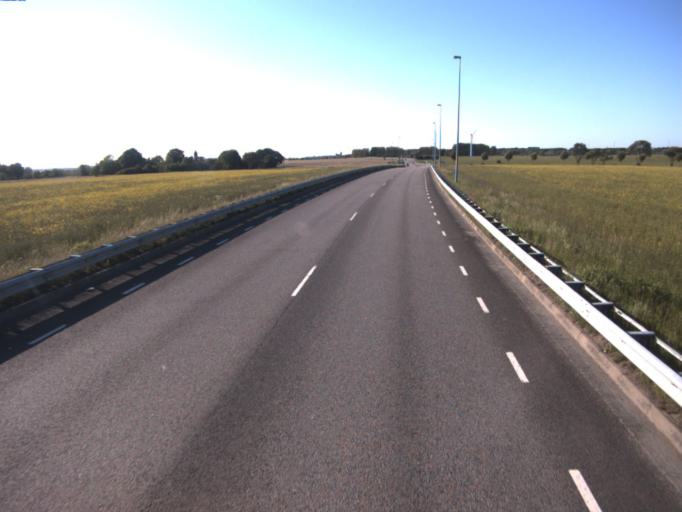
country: SE
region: Skane
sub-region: Helsingborg
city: Rydeback
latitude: 55.9864
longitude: 12.7666
